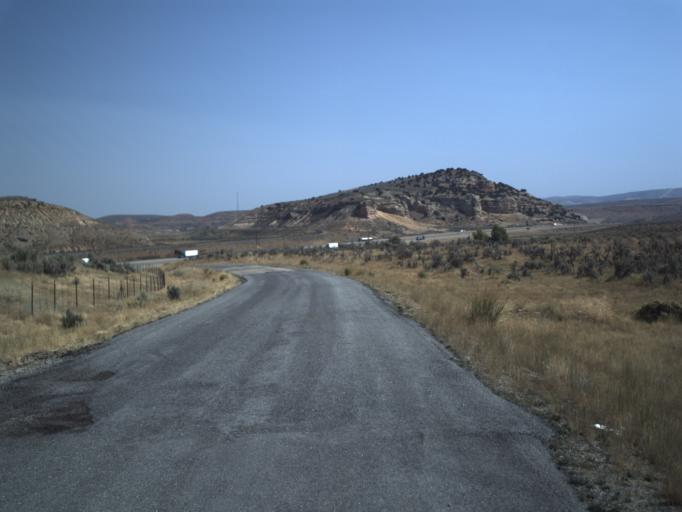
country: US
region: Wyoming
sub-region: Uinta County
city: Evanston
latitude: 41.1188
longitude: -111.1891
